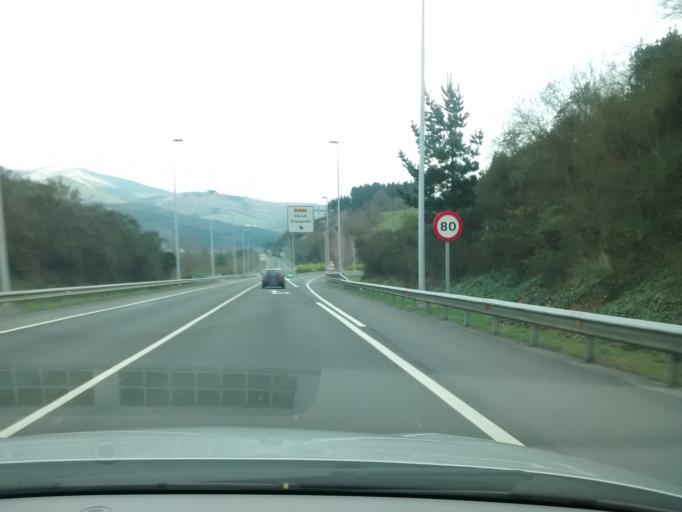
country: ES
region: Basque Country
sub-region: Bizkaia
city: El Corrillo
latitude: 43.2054
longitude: -3.1244
